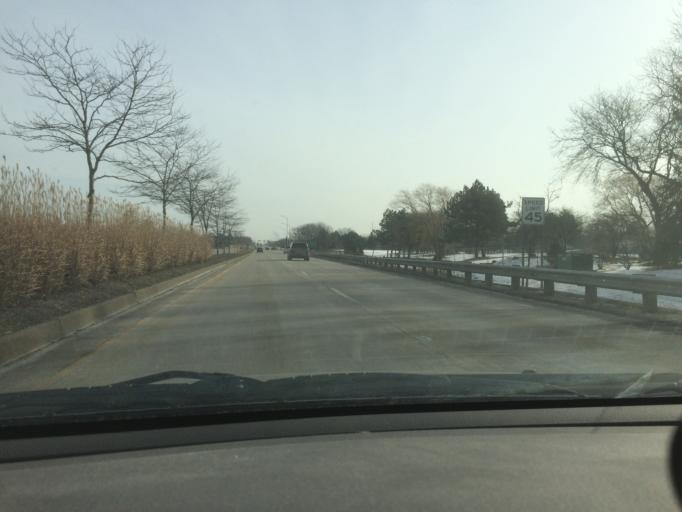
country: US
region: Illinois
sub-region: Cook County
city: South Barrington
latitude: 42.0470
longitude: -88.1315
